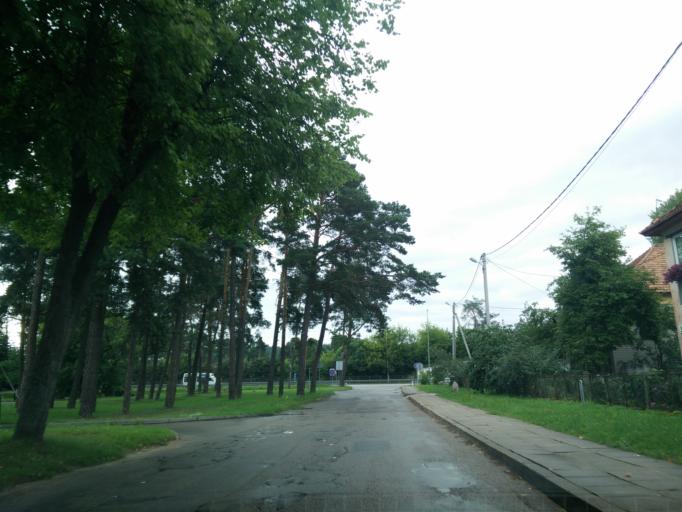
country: LT
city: Grigiskes
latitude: 54.6730
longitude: 25.0904
